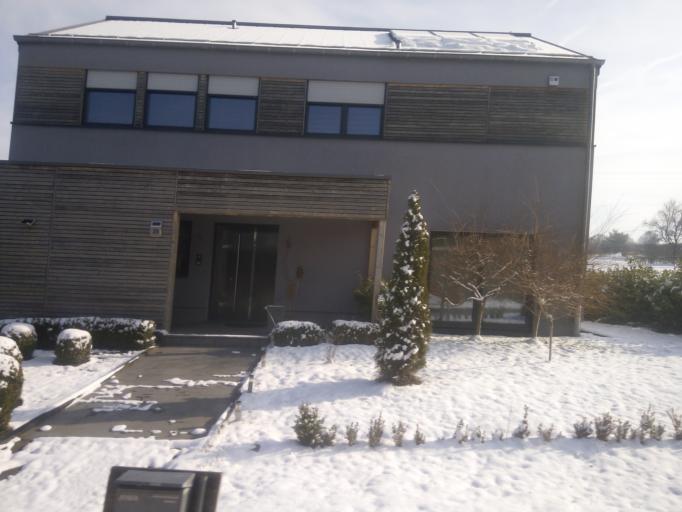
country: LU
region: Grevenmacher
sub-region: Canton d'Echternach
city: Consdorf
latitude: 49.7546
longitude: 6.3274
